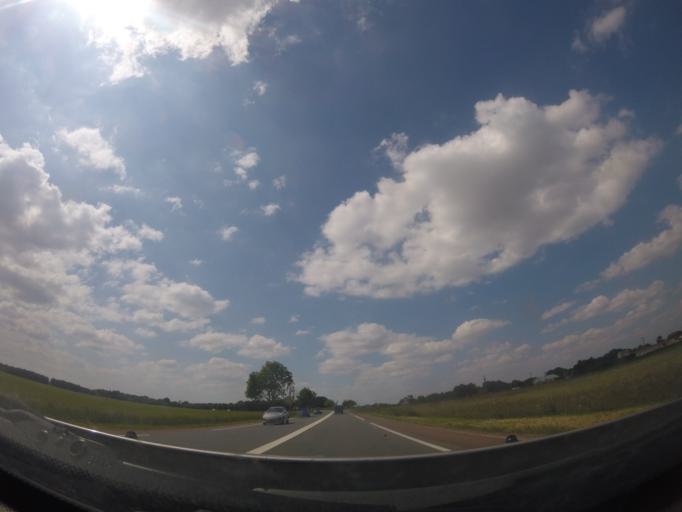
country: FR
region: Poitou-Charentes
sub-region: Departement de la Charente-Maritime
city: Saint-Porchaire
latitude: 45.8380
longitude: -0.8074
